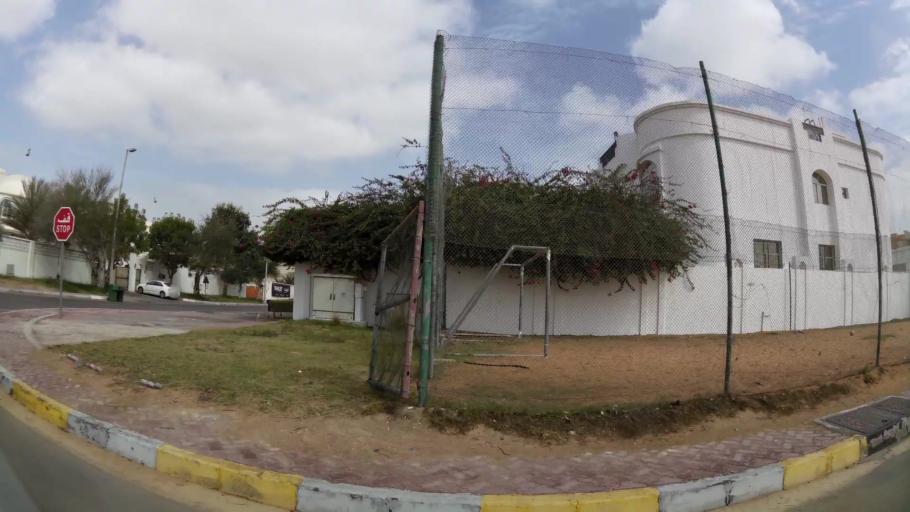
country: AE
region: Abu Dhabi
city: Abu Dhabi
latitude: 24.4044
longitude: 54.5157
